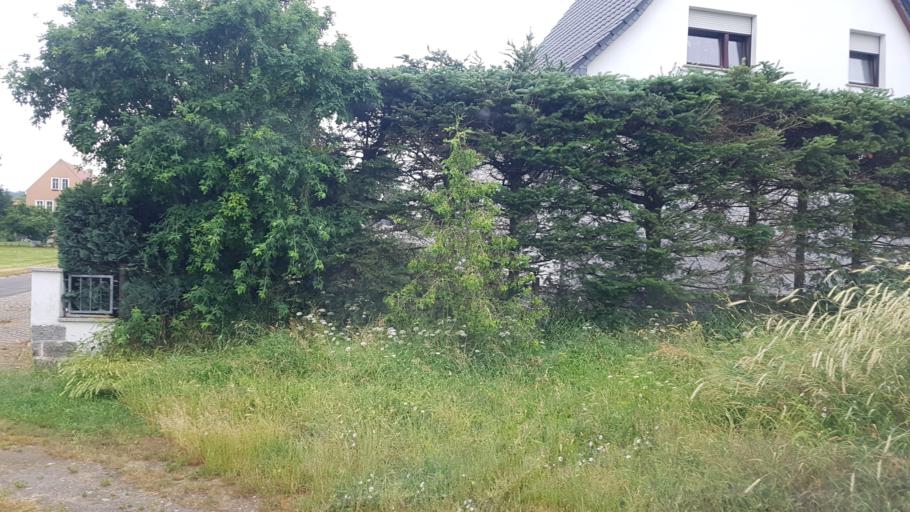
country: DE
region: Brandenburg
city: Grosskmehlen
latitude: 51.3821
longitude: 13.7233
